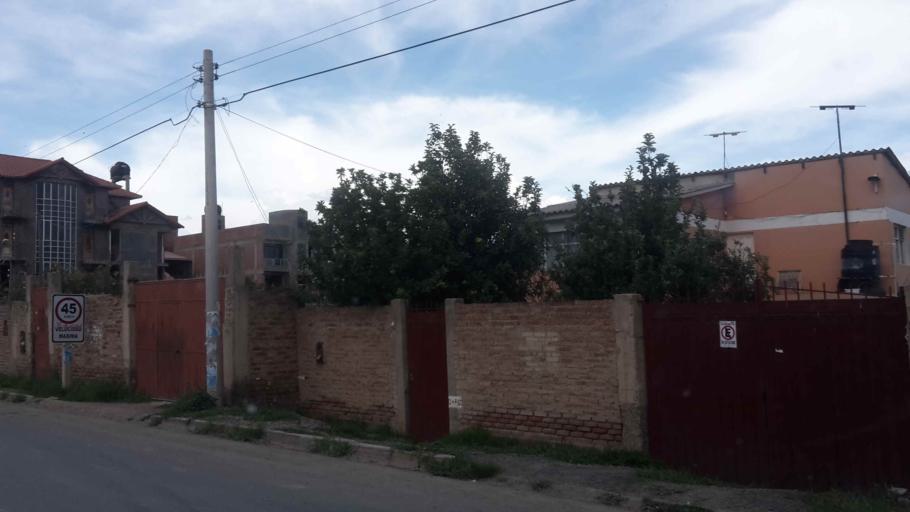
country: BO
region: Cochabamba
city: Sipe Sipe
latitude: -17.4090
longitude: -66.2863
